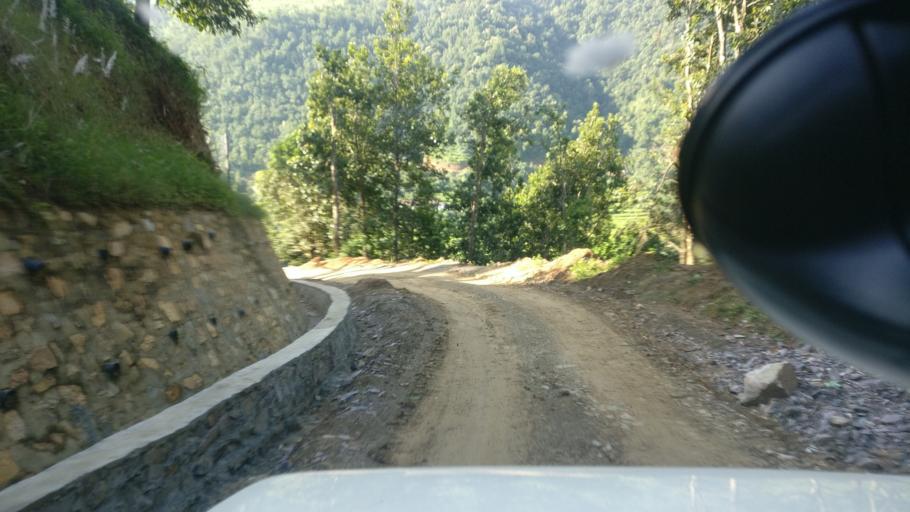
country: NP
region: Western Region
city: Baglung
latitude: 28.1483
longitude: 83.6580
